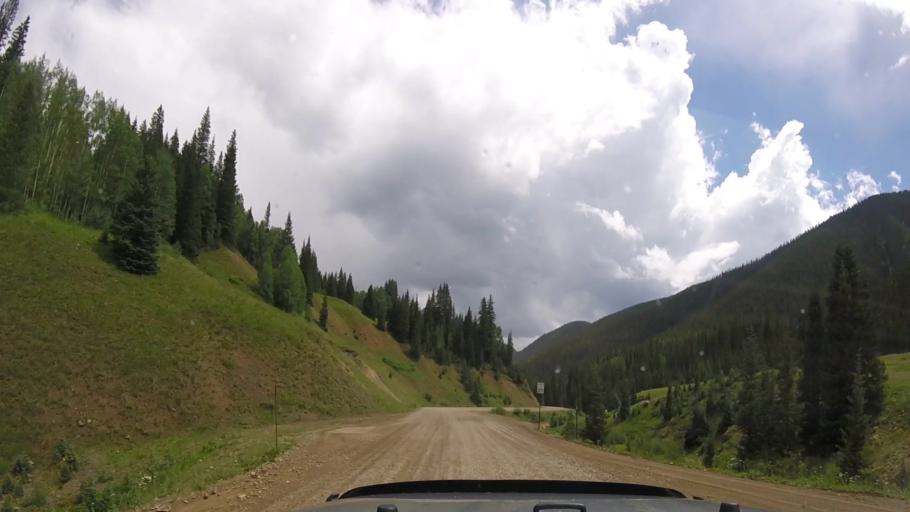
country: US
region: Colorado
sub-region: San Juan County
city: Silverton
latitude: 37.8412
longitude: -107.6798
